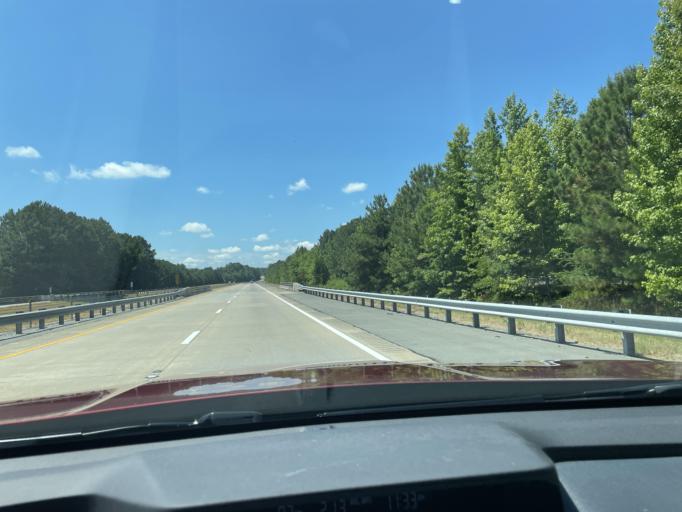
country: US
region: Arkansas
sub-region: Jefferson County
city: Redfield
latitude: 34.4824
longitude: -92.2085
